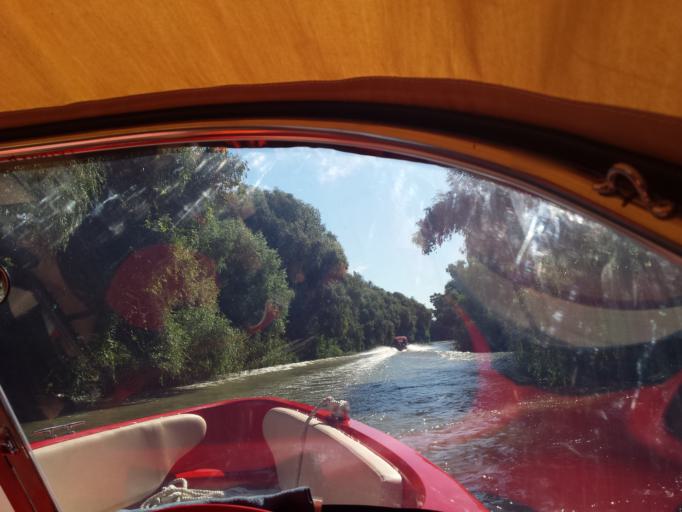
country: RO
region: Tulcea
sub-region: Comuna Pardina
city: Pardina
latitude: 45.2485
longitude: 29.0334
